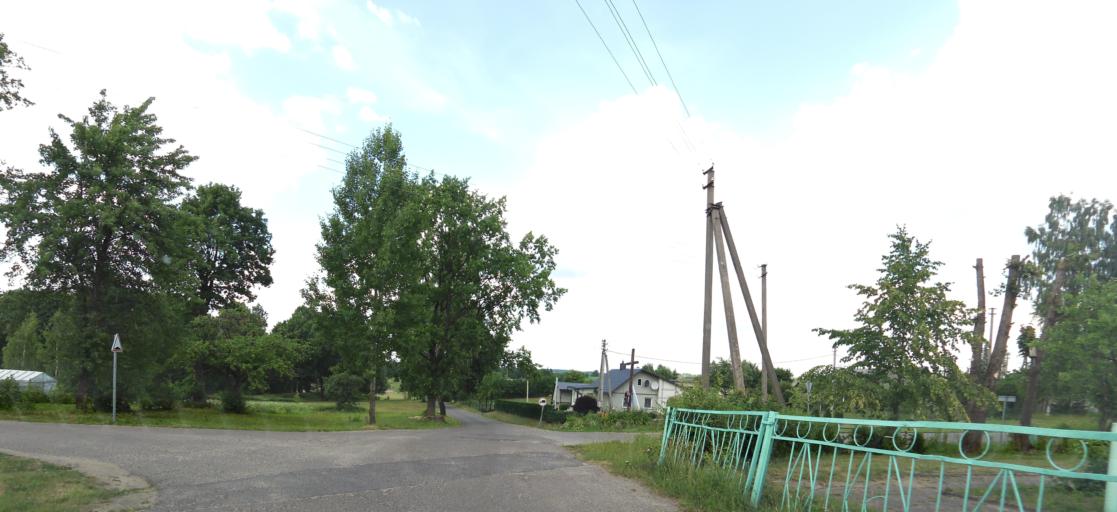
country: LT
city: Skaidiskes
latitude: 54.5370
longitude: 25.6517
